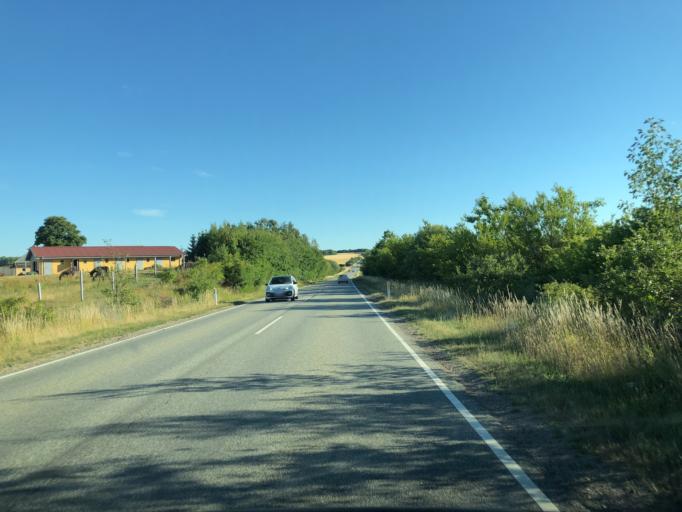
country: DK
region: Central Jutland
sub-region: Arhus Kommune
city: Framlev
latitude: 56.1307
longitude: 9.9963
